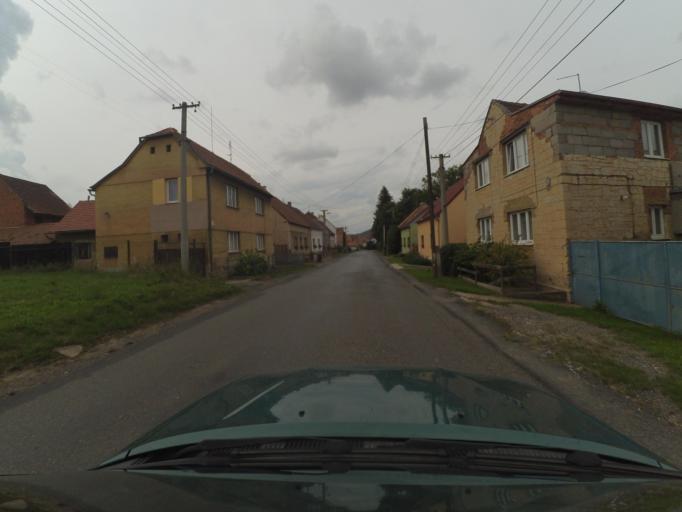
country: CZ
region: Central Bohemia
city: Revnicov
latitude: 50.1916
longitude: 13.7477
